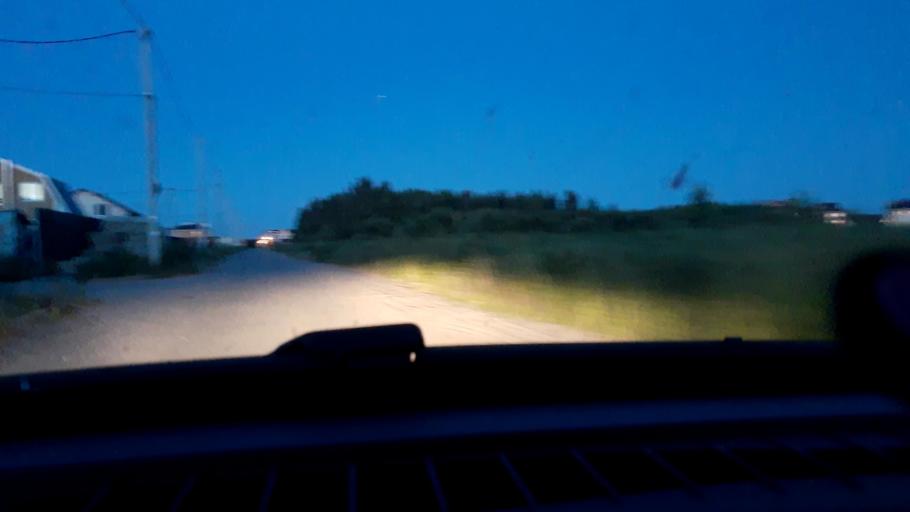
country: RU
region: Nizjnij Novgorod
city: Bor
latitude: 56.3930
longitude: 44.0647
